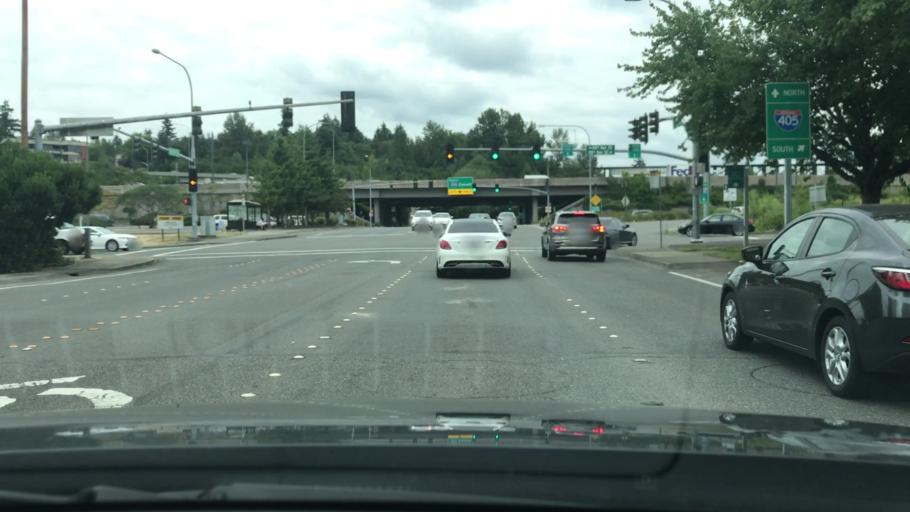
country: US
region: Washington
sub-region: King County
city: Bellevue
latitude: 47.6022
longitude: -122.1860
